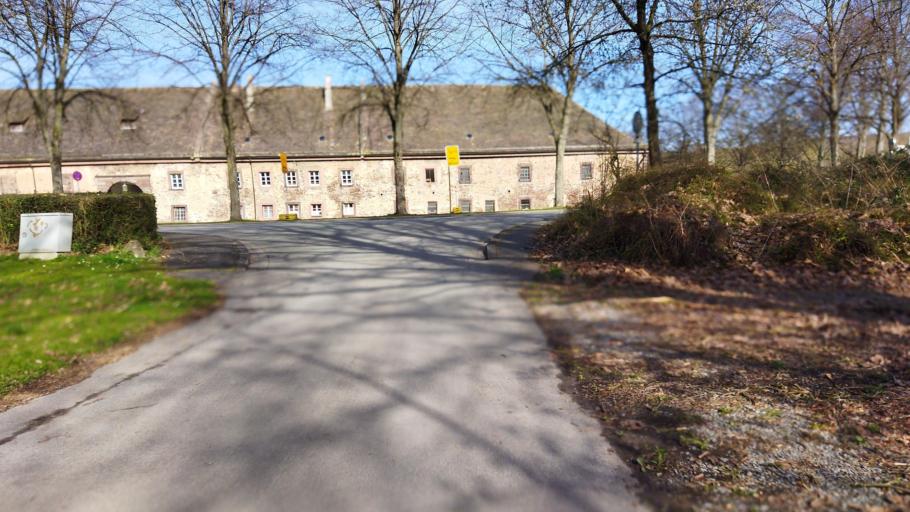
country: DE
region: North Rhine-Westphalia
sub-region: Regierungsbezirk Detmold
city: Hoexter
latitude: 51.7769
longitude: 9.4070
